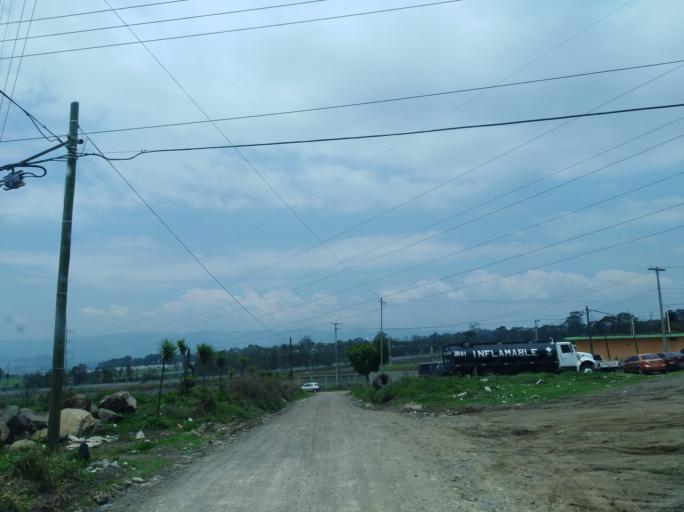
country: GT
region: Guatemala
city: Villa Nueva
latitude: 14.5228
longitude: -90.6208
